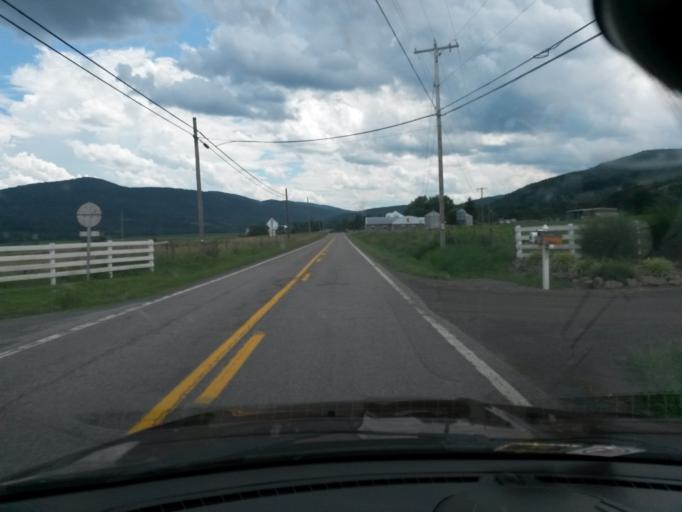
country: US
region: West Virginia
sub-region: Pendleton County
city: Franklin
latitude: 38.7804
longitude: -79.2840
